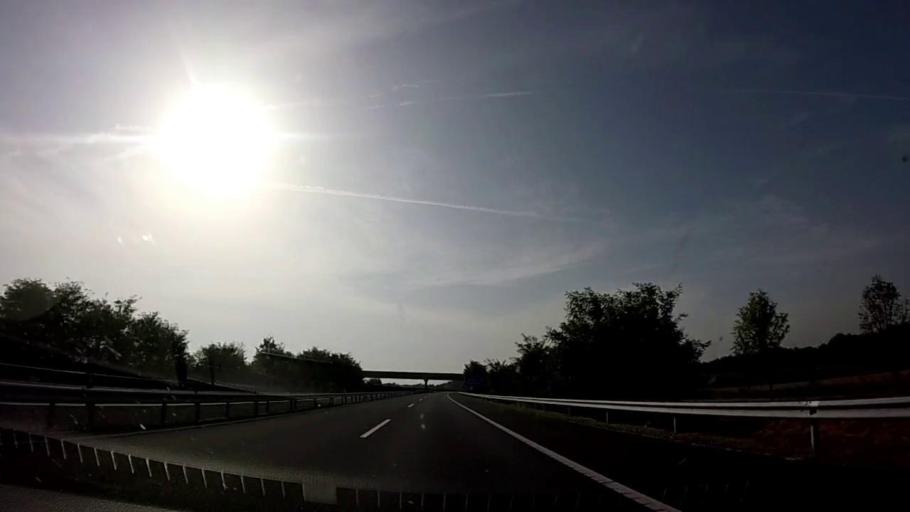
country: HU
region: Zala
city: Zalakomar
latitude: 46.5805
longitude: 17.2516
